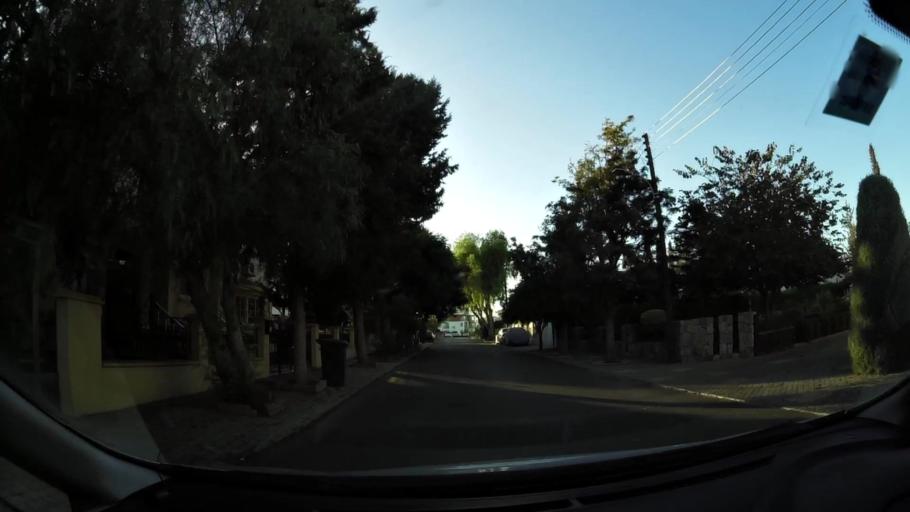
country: CY
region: Lefkosia
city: Nicosia
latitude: 35.2040
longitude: 33.3246
